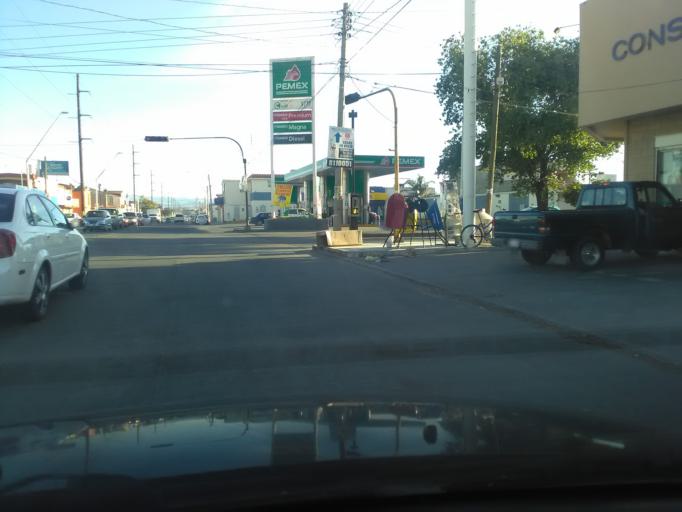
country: MX
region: Durango
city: Victoria de Durango
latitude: 24.0203
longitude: -104.6329
